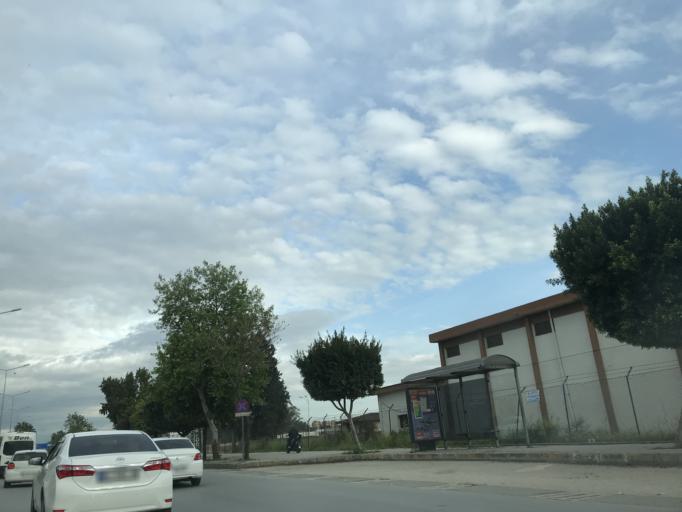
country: TR
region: Adana
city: Seyhan
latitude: 36.9942
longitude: 35.2890
